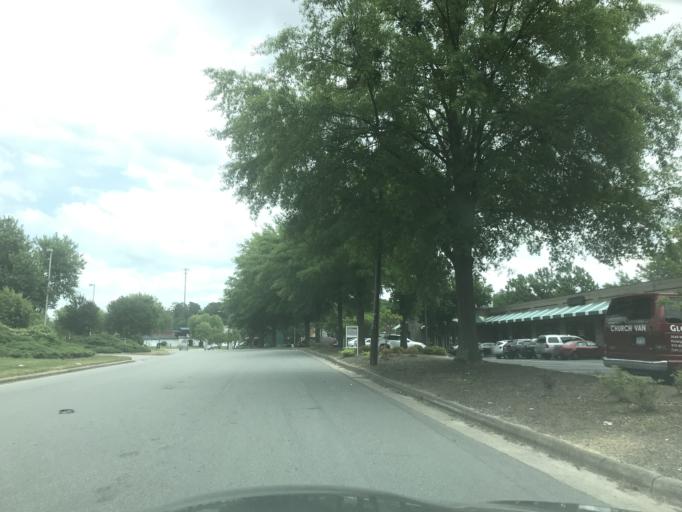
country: US
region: North Carolina
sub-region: Wake County
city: Raleigh
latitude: 35.7967
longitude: -78.5825
